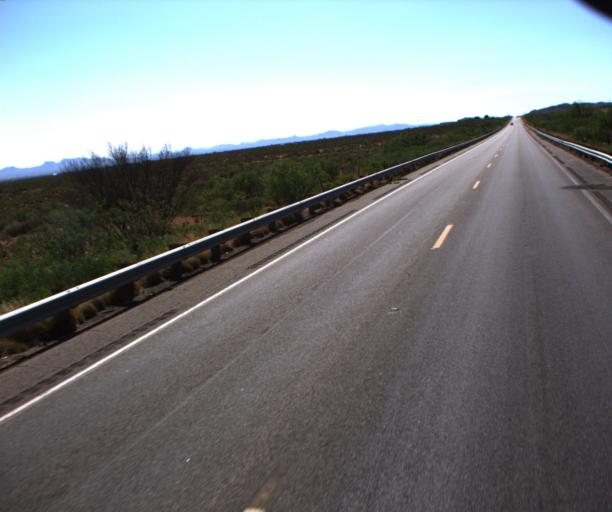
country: US
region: Arizona
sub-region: Cochise County
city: Bisbee
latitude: 31.4082
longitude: -109.7844
